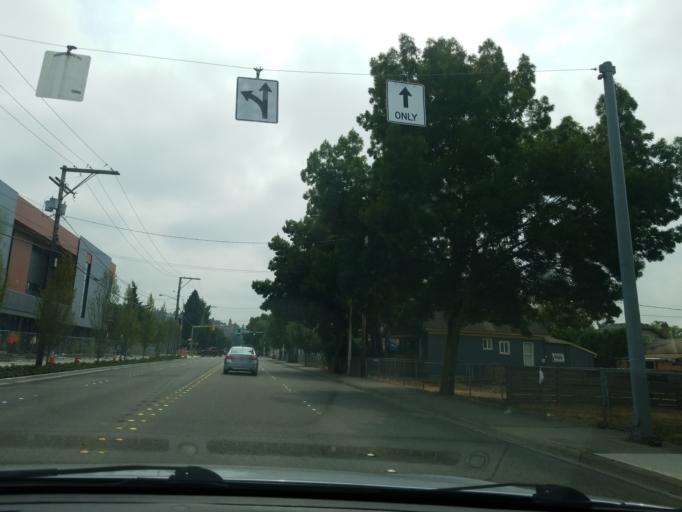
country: US
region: Washington
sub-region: King County
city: Renton
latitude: 47.4878
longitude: -122.2022
